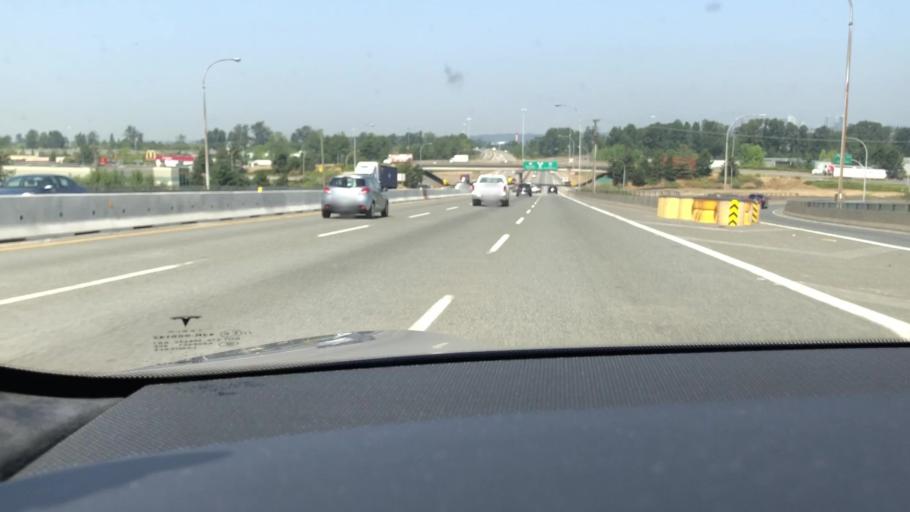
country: CA
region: British Columbia
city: Delta
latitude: 49.1689
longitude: -122.9480
